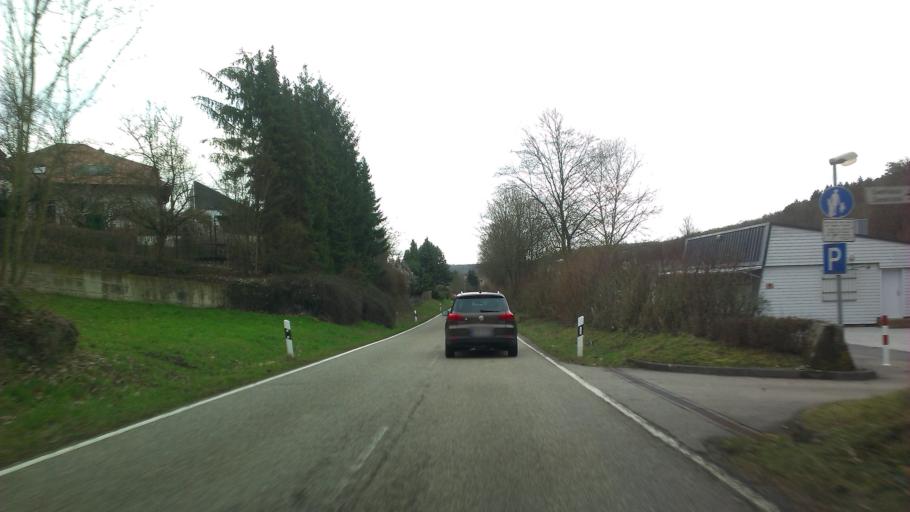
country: DE
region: Baden-Wuerttemberg
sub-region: Regierungsbezirk Stuttgart
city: Eppingen
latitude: 49.0942
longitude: 8.8994
